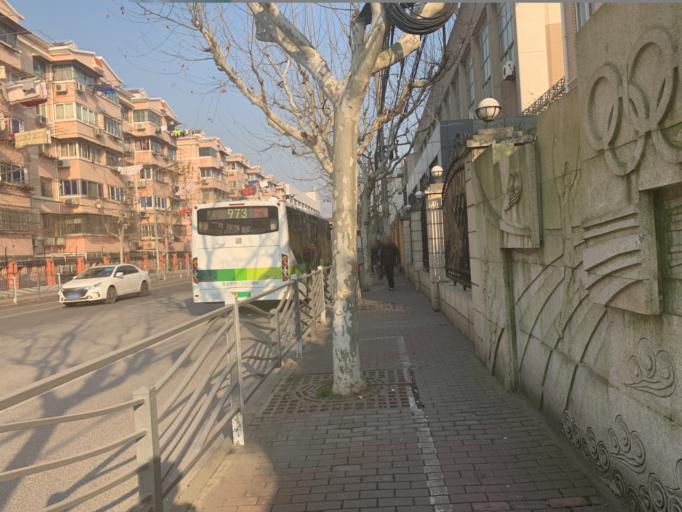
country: CN
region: Shanghai Shi
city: Changqiao
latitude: 31.1442
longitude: 121.4261
